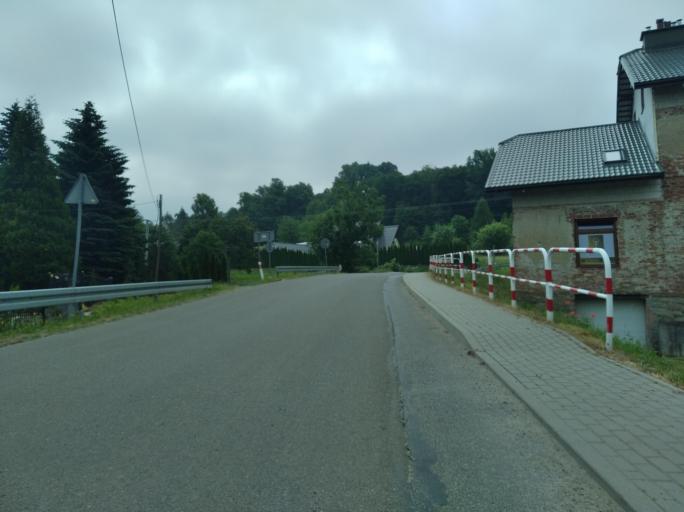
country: PL
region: Subcarpathian Voivodeship
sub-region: Powiat sanocki
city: Besko
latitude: 49.5884
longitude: 21.9466
